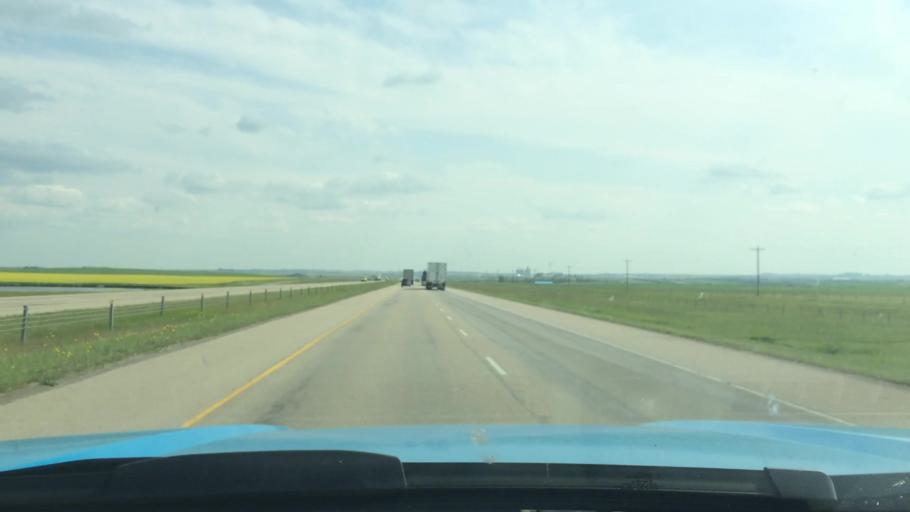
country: CA
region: Alberta
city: Carstairs
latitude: 51.5322
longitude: -114.0254
